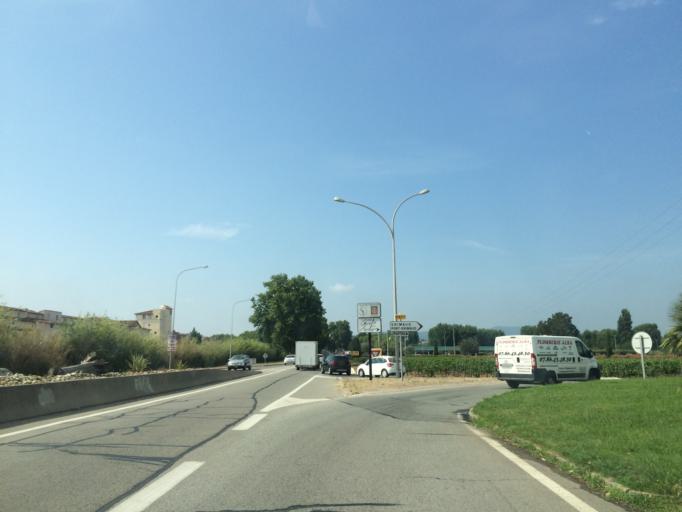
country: FR
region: Provence-Alpes-Cote d'Azur
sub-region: Departement du Var
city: Gassin
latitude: 43.2737
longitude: 6.5742
